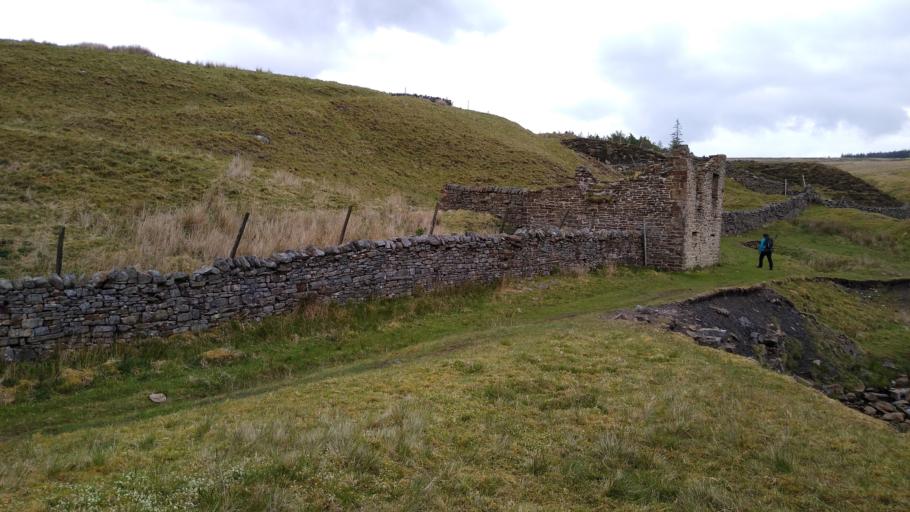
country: GB
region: England
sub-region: Northumberland
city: Bardon Mill
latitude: 54.7773
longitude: -2.3824
